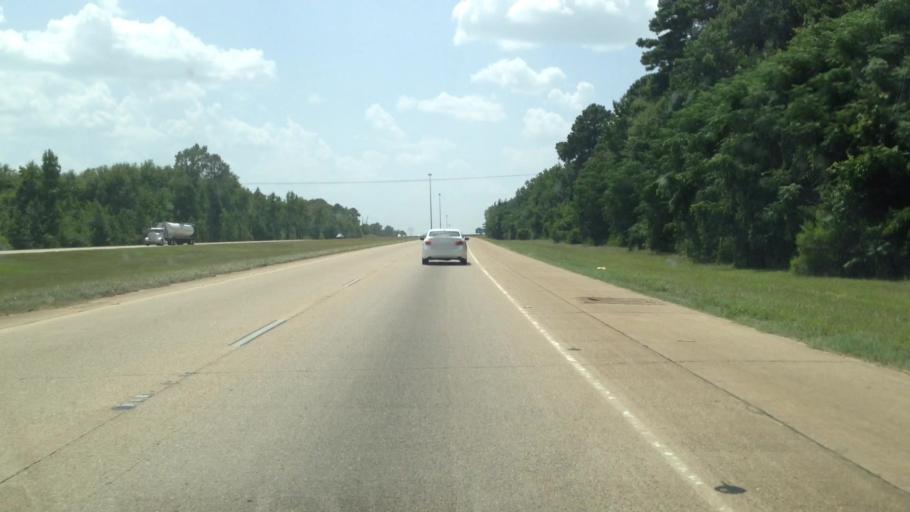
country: US
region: Louisiana
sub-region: Lincoln Parish
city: Grambling
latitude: 32.5407
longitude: -92.7027
